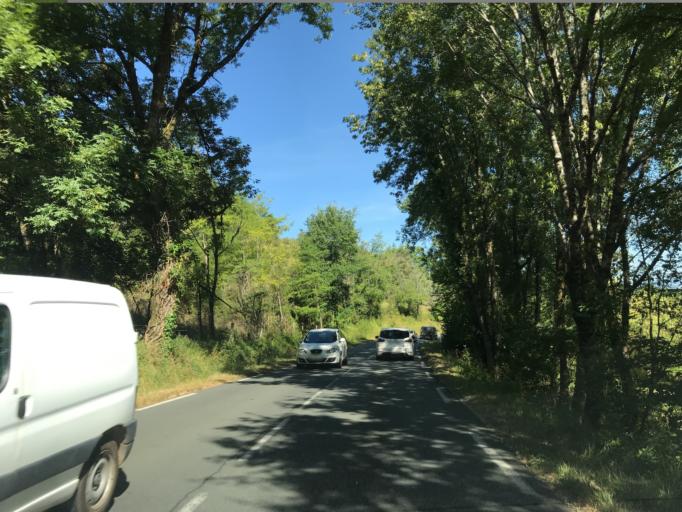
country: FR
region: Limousin
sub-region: Departement de la Correze
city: Larche
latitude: 45.1015
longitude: 1.3877
